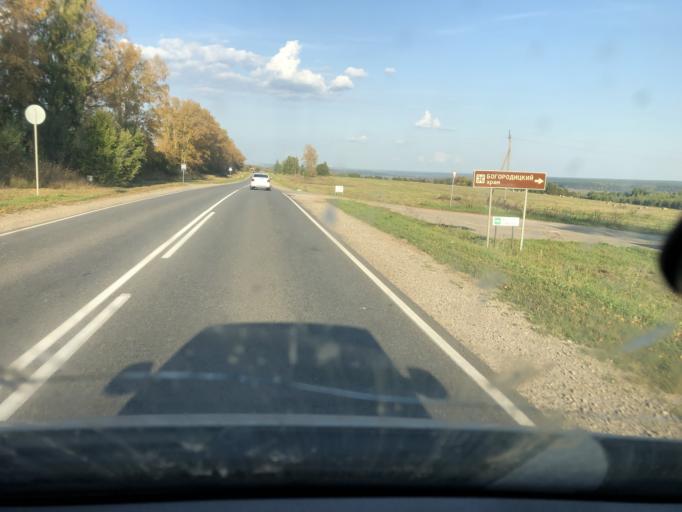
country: RU
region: Kaluga
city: Sosenskiy
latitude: 54.2084
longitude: 35.9714
